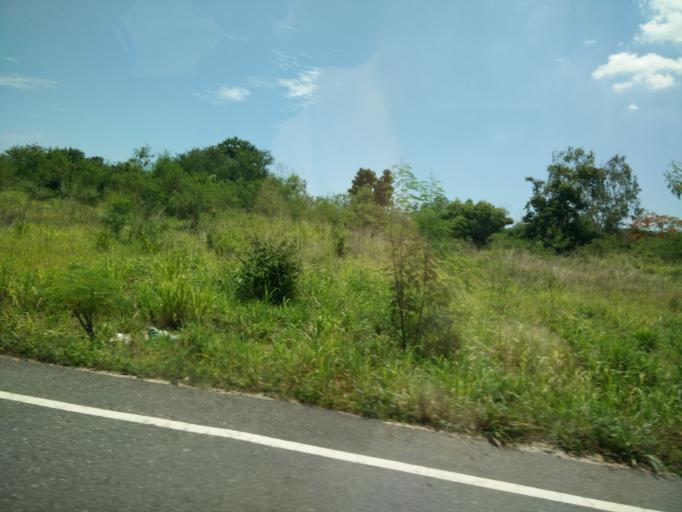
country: TH
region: Chon Buri
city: Phatthaya
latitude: 12.9049
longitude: 100.9879
